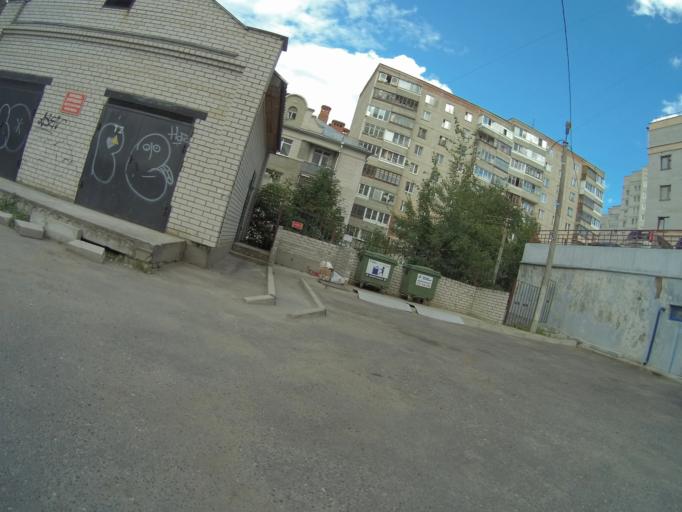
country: RU
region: Vladimir
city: Vladimir
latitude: 56.1196
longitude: 40.3518
